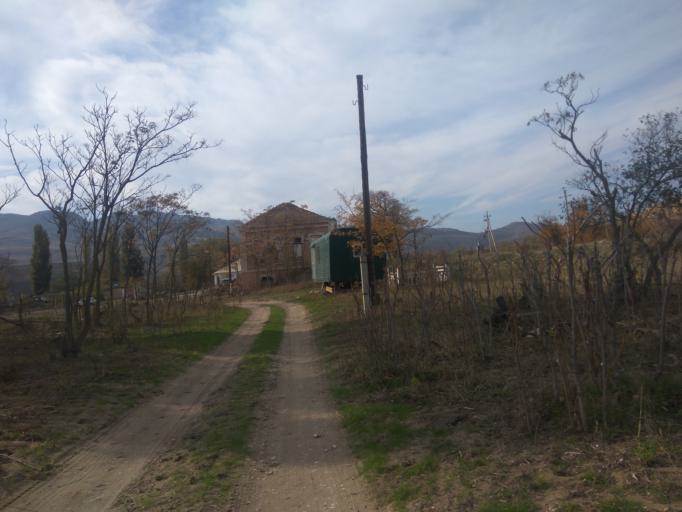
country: RU
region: Dagestan
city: Korkmaskala
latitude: 43.0035
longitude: 47.2388
